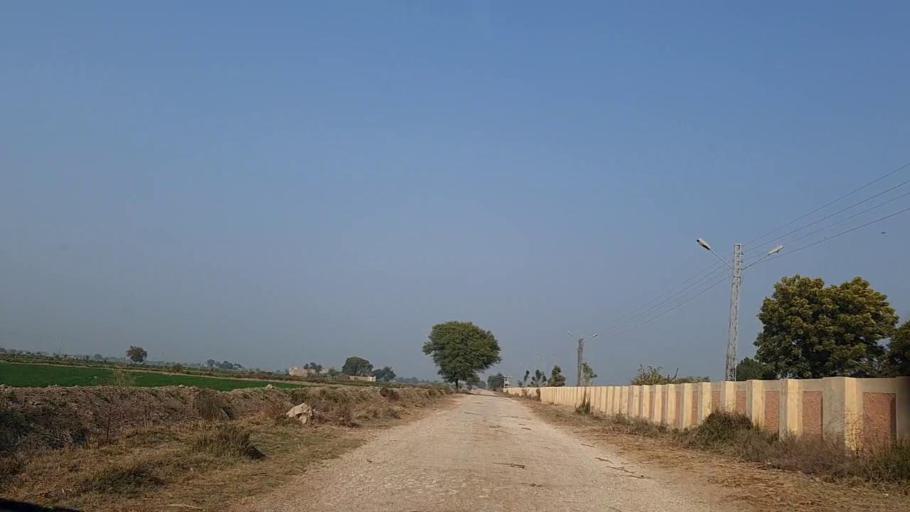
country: PK
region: Sindh
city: Sann
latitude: 26.1848
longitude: 68.1107
